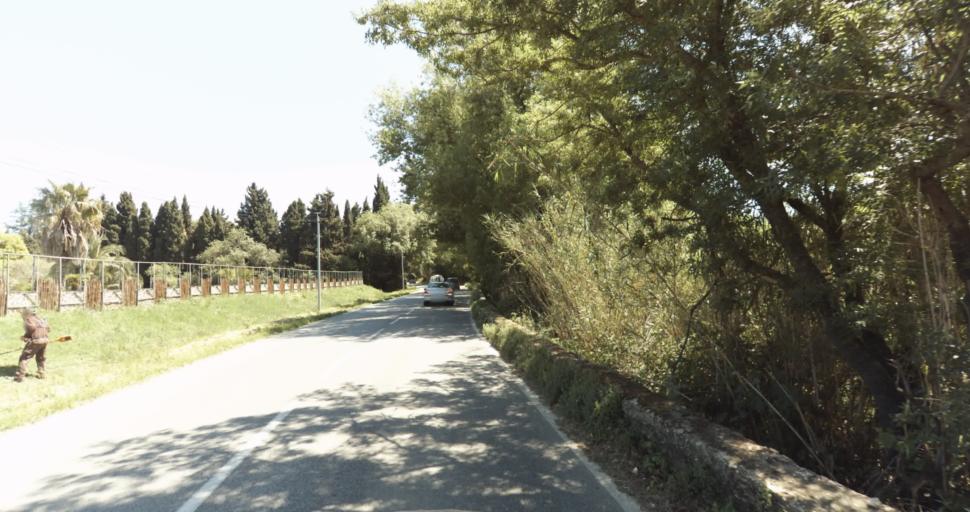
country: FR
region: Provence-Alpes-Cote d'Azur
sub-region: Departement du Var
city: Hyeres
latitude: 43.1325
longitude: 6.1633
